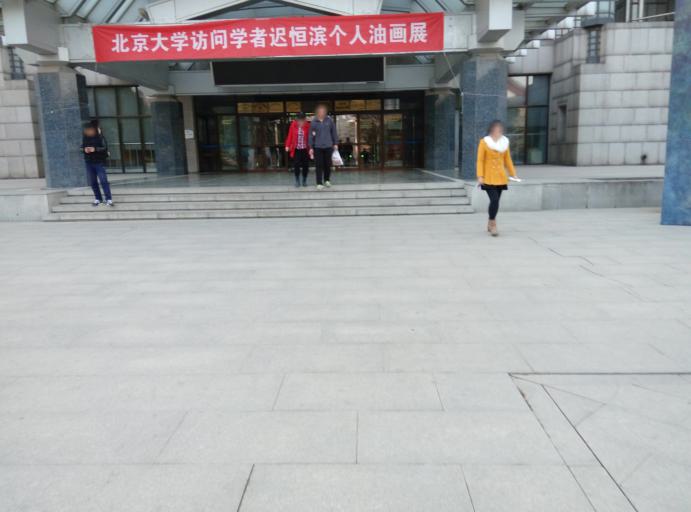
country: CN
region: Beijing
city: Haidian
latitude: 39.9907
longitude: 116.3047
